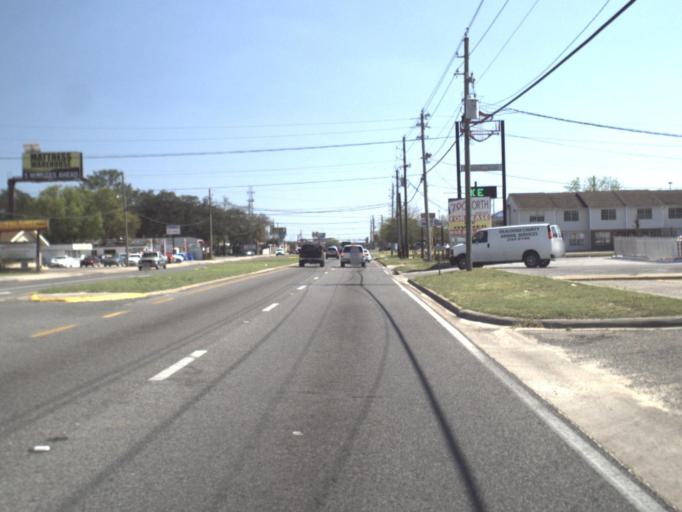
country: US
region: Florida
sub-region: Okaloosa County
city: Wright
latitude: 30.4465
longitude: -86.6387
